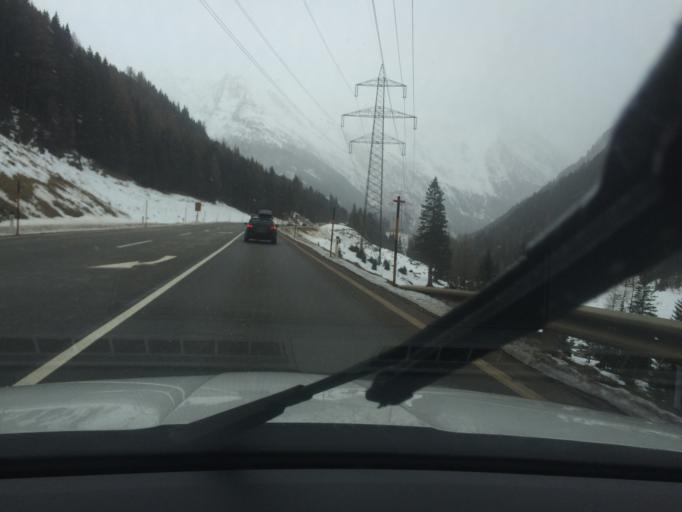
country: AT
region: Tyrol
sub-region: Politischer Bezirk Lienz
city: Matrei in Osttirol
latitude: 47.1033
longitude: 12.5081
